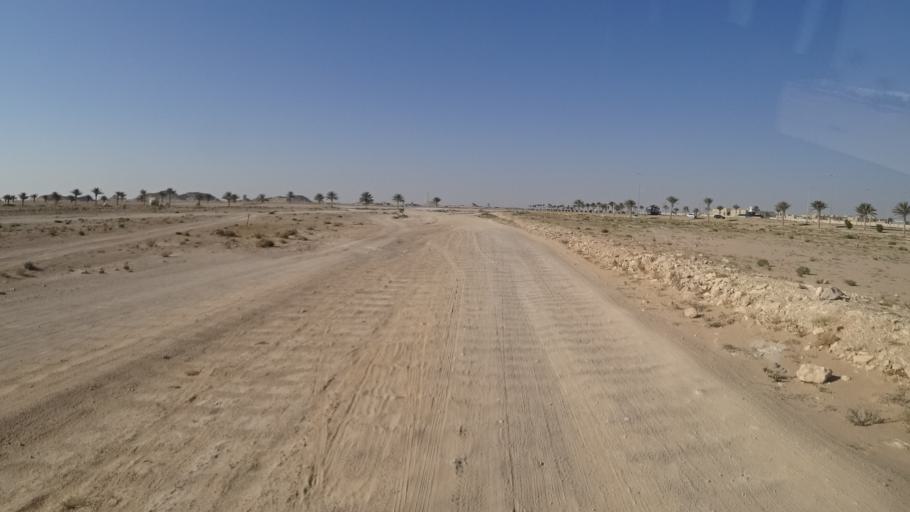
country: OM
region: Zufar
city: Salalah
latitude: 17.6101
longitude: 54.0320
